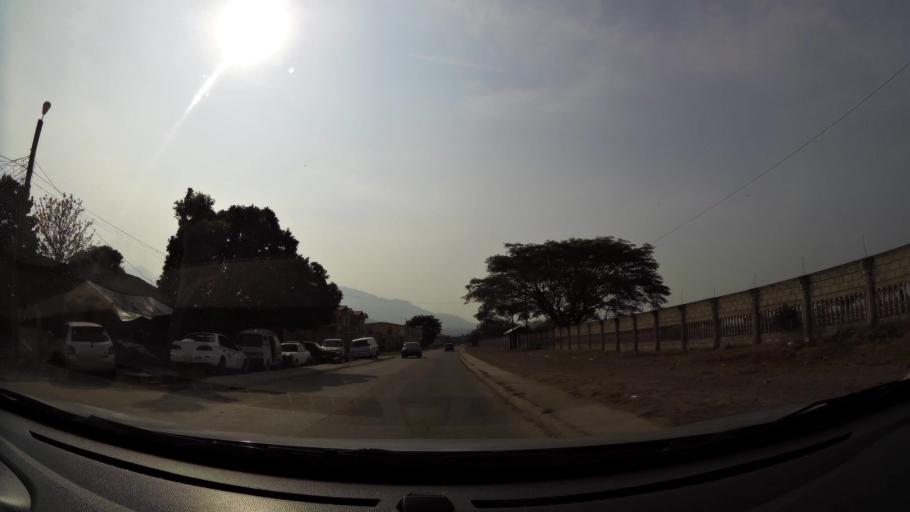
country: HN
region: Comayagua
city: Comayagua
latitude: 14.4523
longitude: -87.6224
